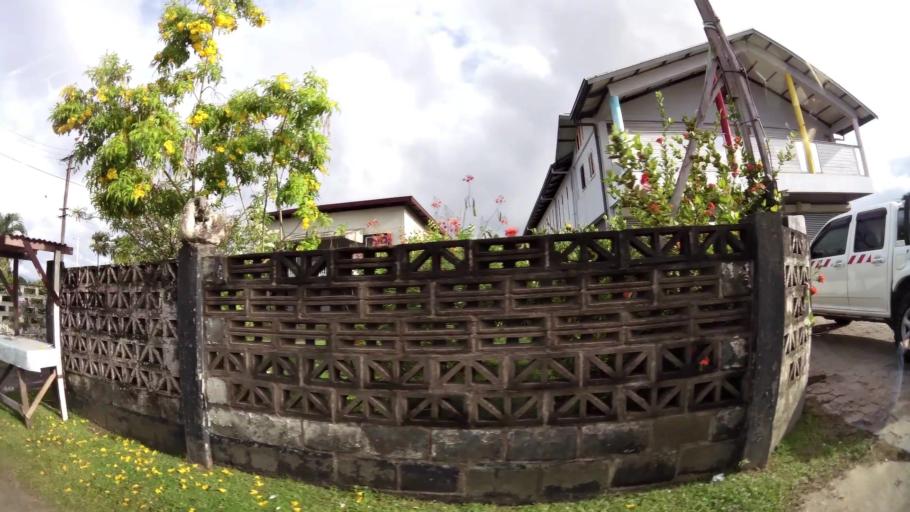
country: SR
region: Paramaribo
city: Paramaribo
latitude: 5.8469
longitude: -55.2361
